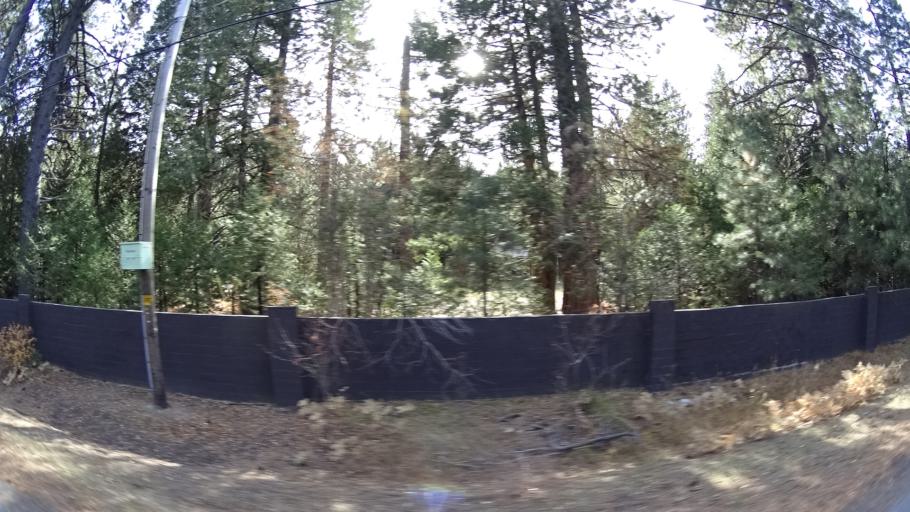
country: US
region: California
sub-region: Siskiyou County
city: Weed
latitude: 41.3821
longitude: -122.3955
